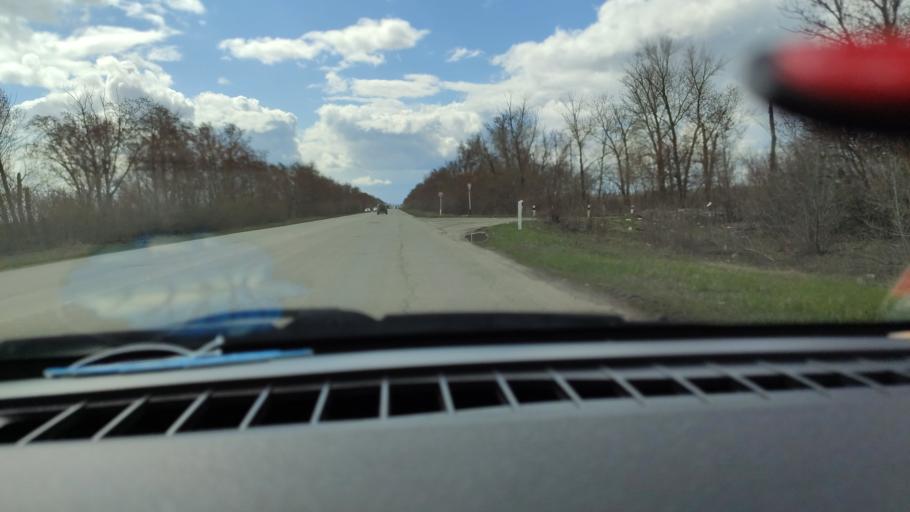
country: RU
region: Samara
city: Tol'yatti
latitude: 53.6001
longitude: 49.4089
